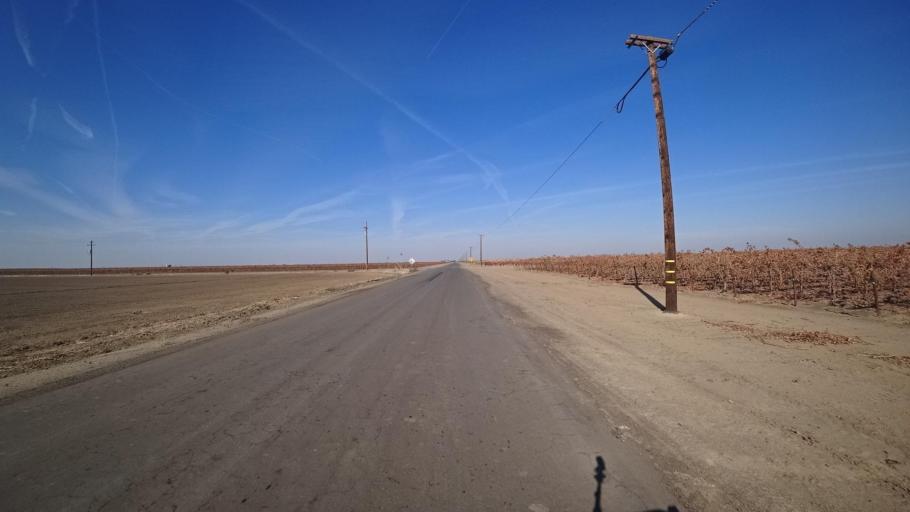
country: US
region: California
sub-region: Kern County
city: Wasco
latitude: 35.6878
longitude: -119.3839
